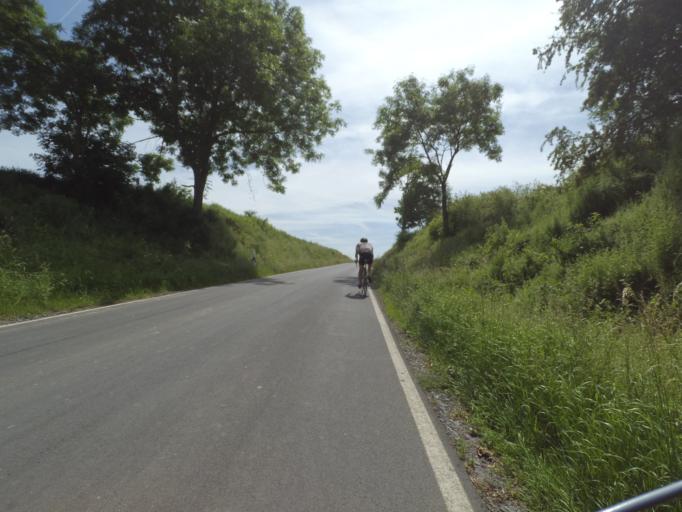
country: DE
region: Rheinland-Pfalz
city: Pillig
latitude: 50.2358
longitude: 7.3145
